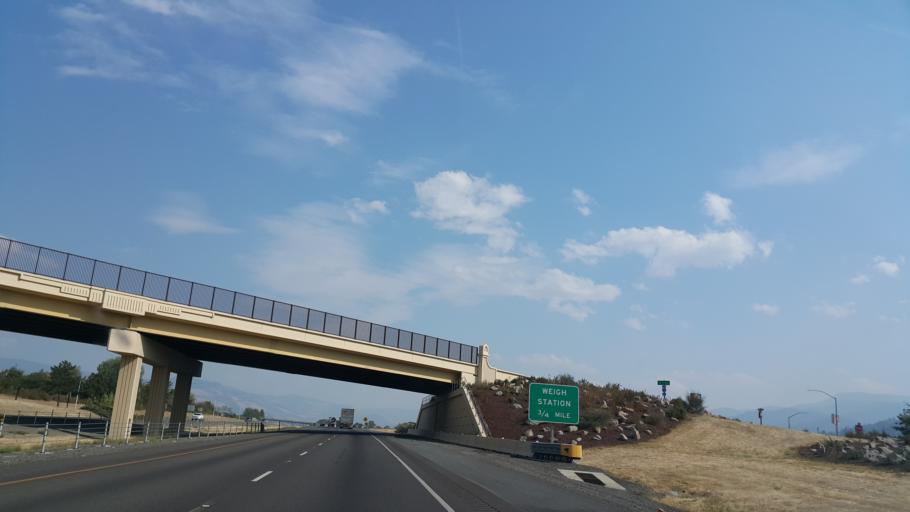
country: US
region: Oregon
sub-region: Jackson County
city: Ashland
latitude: 42.2280
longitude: -122.7421
